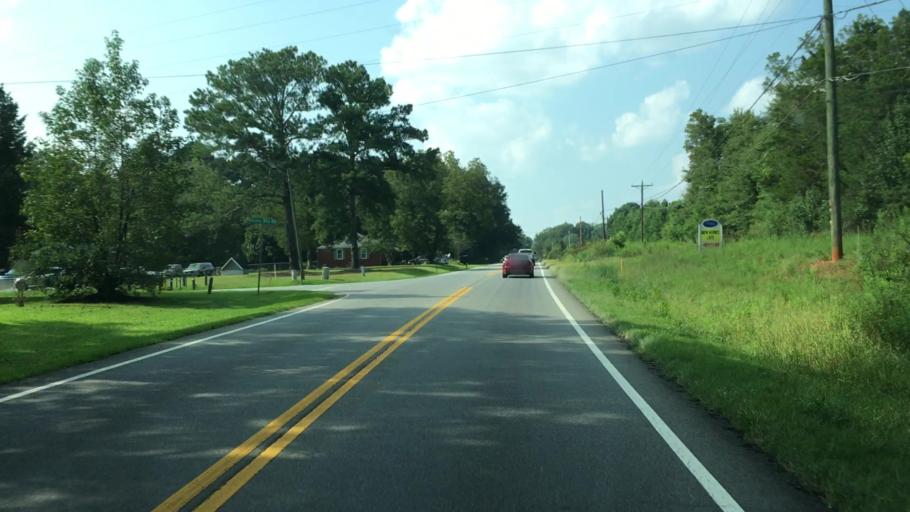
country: US
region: Georgia
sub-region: Walton County
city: Monroe
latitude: 33.7362
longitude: -83.7018
